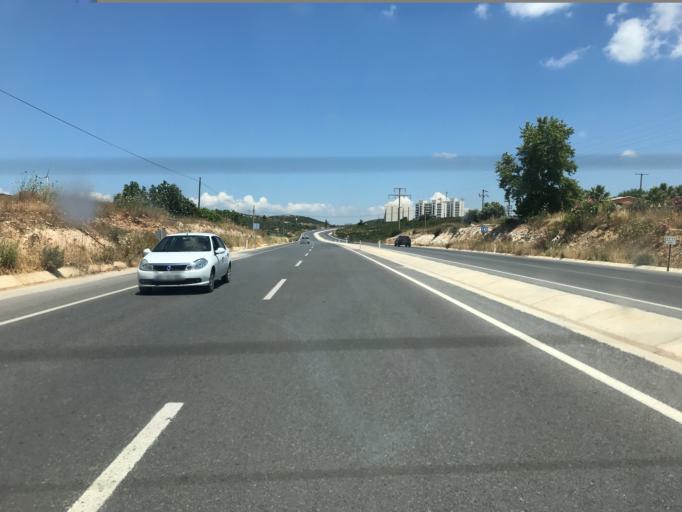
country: TR
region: Aydin
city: Akkoy
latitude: 37.4697
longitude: 27.3393
